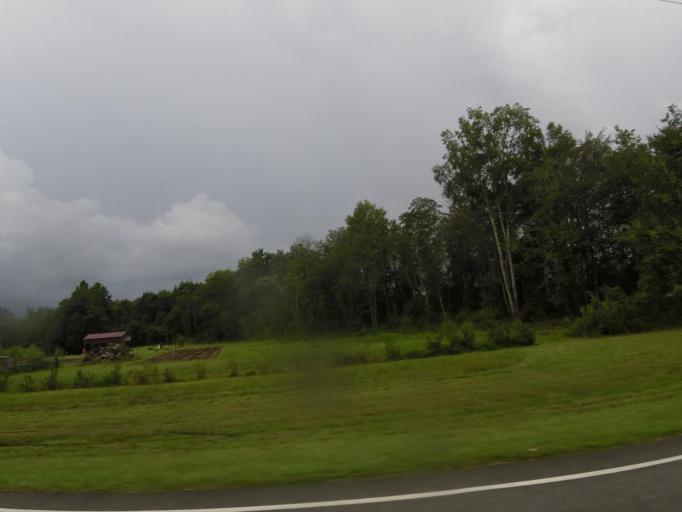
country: US
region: Florida
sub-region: Baker County
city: Macclenny
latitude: 30.4071
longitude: -82.1873
